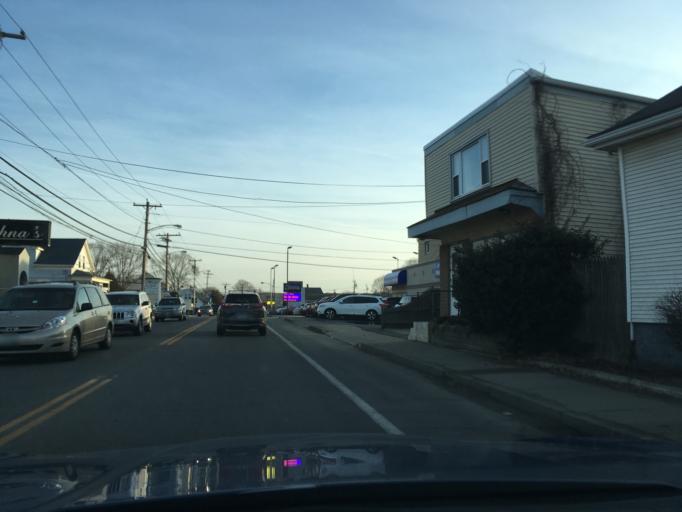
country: US
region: Rhode Island
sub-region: Providence County
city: North Providence
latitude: 41.8314
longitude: -71.4736
